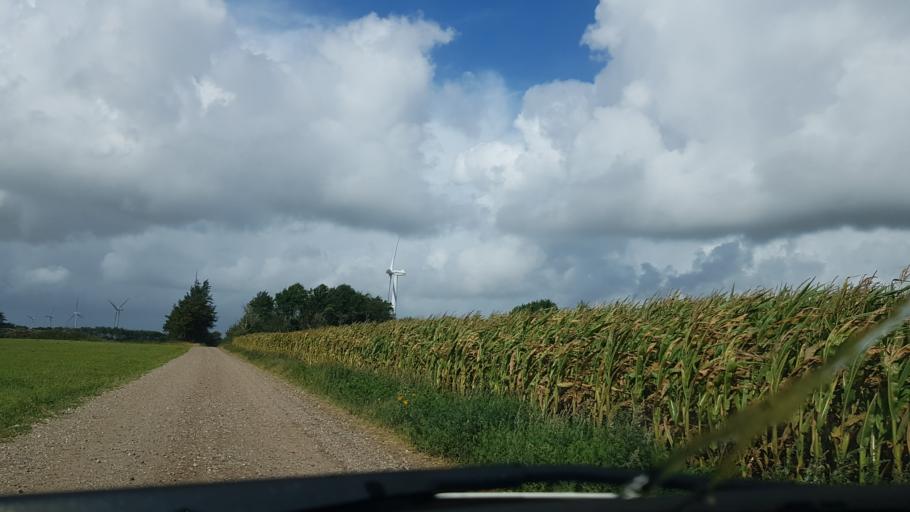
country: DK
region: South Denmark
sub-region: Esbjerg Kommune
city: Ribe
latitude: 55.2452
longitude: 8.7783
